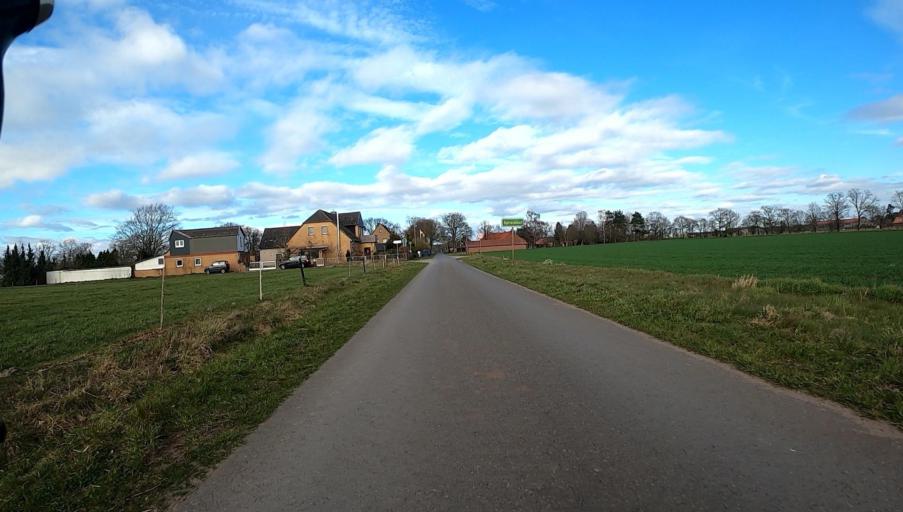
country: DE
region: Lower Saxony
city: Lindwedel
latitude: 52.6062
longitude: 9.7150
